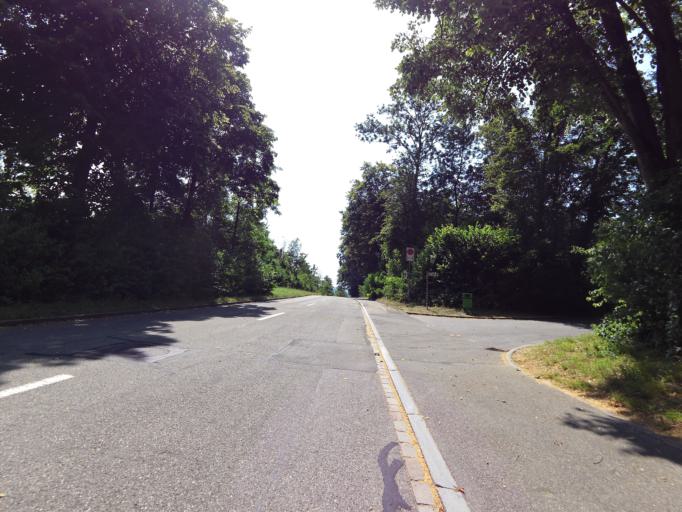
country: CH
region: Aargau
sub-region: Bezirk Baden
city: Birmenstorf
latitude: 47.4580
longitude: 8.2767
